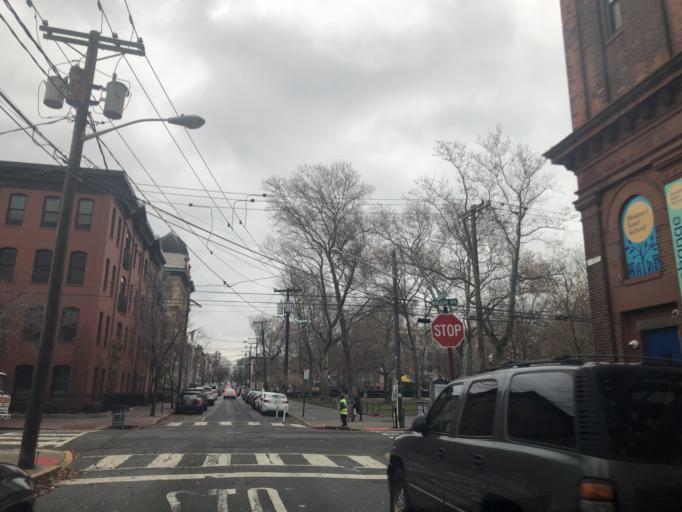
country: US
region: New Jersey
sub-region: Hudson County
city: Hoboken
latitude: 40.7429
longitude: -74.0333
